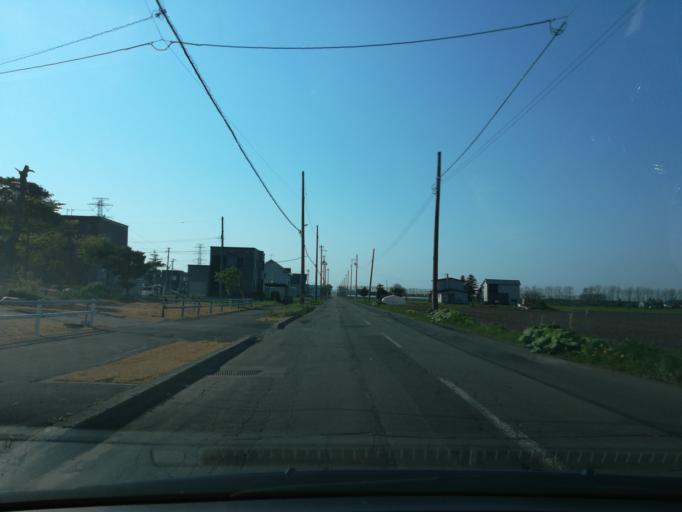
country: JP
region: Hokkaido
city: Ebetsu
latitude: 43.1305
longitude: 141.6171
